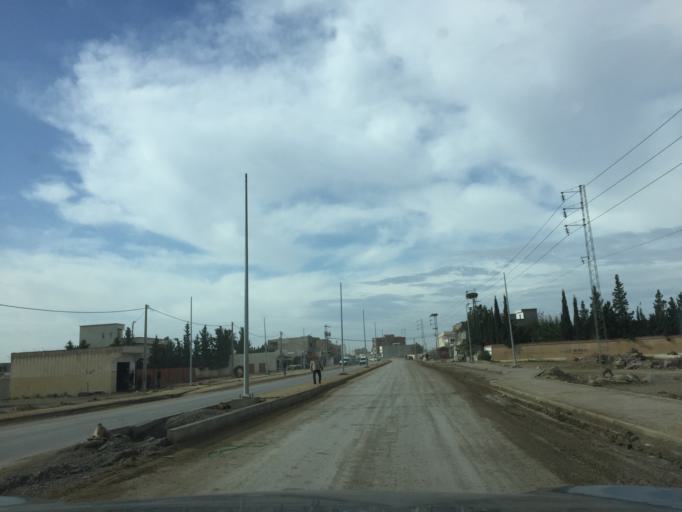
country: TN
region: Zaghwan
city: El Fahs
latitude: 36.3698
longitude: 9.8989
